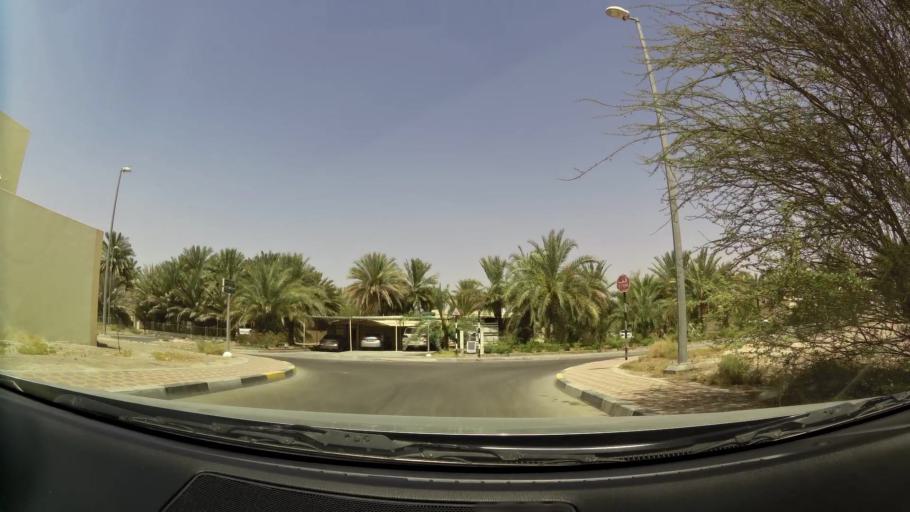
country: OM
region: Al Buraimi
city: Al Buraymi
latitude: 24.2822
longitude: 55.7774
